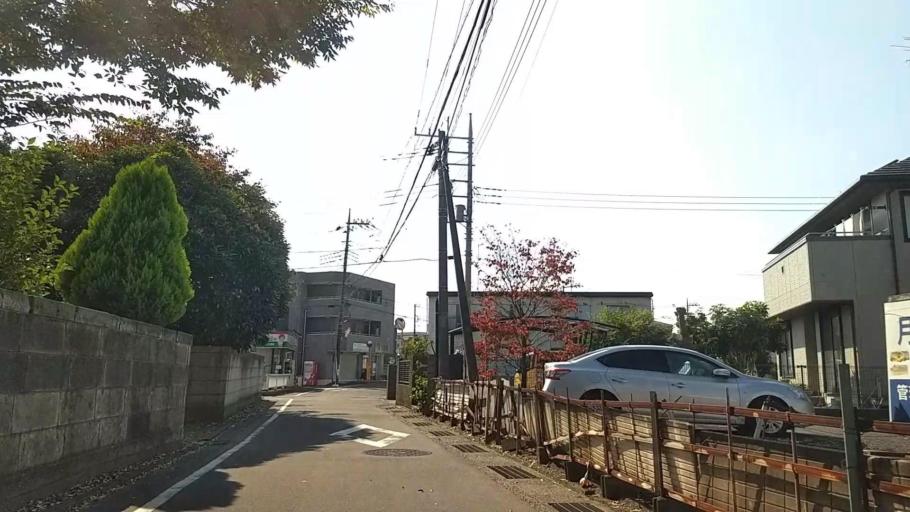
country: JP
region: Kanagawa
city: Atsugi
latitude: 35.4556
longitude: 139.3620
